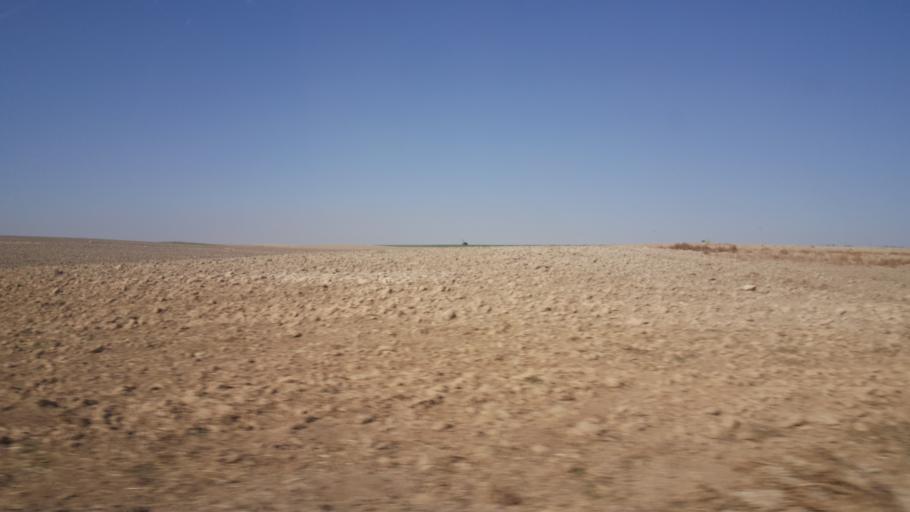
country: TR
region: Konya
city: Celtik
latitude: 39.0627
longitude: 31.8769
